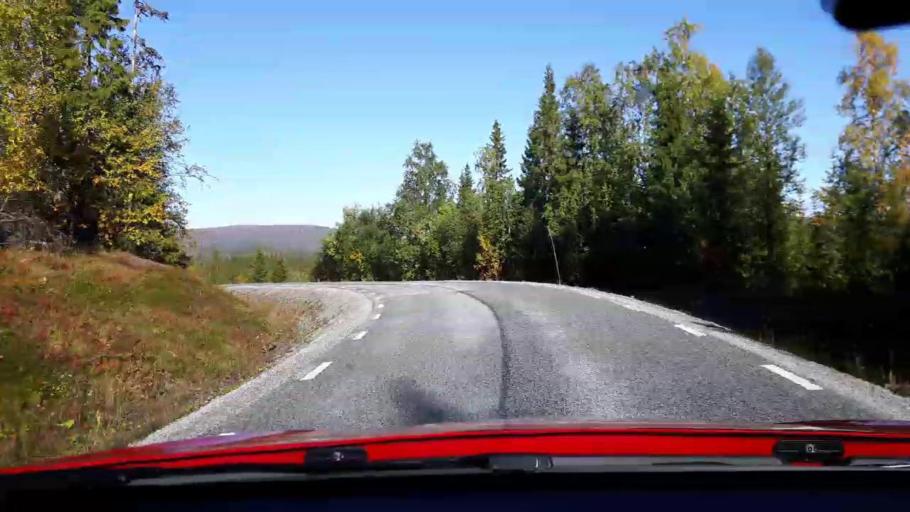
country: NO
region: Nord-Trondelag
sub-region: Lierne
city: Sandvika
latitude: 64.6221
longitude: 13.6966
